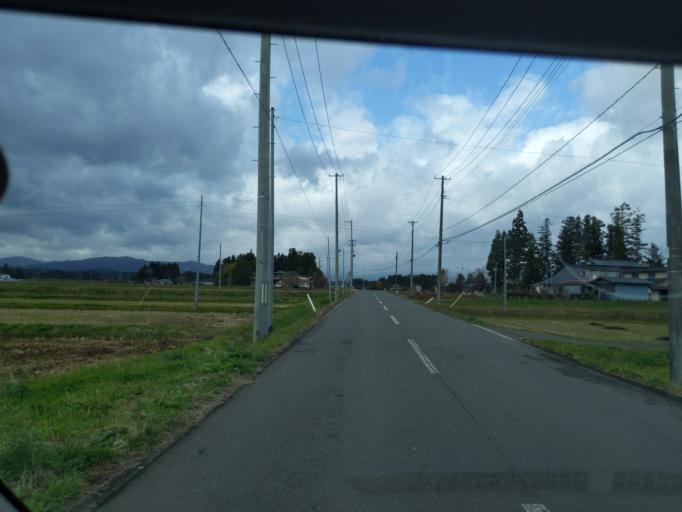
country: JP
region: Iwate
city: Mizusawa
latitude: 39.0632
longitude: 141.0992
